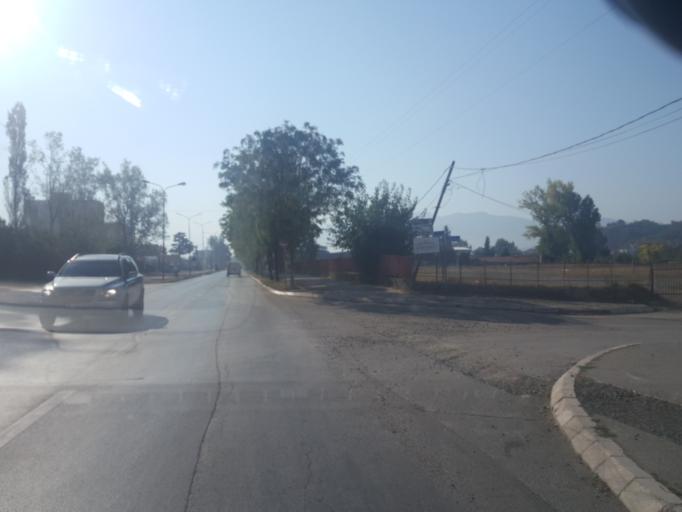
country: XK
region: Gjakova
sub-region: Komuna e Gjakoves
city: Gjakove
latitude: 42.3972
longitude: 20.4192
